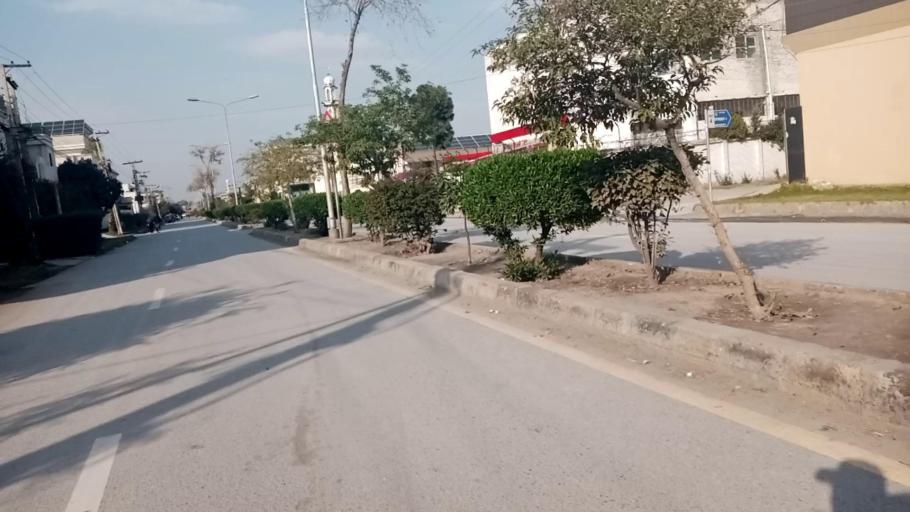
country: PK
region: Khyber Pakhtunkhwa
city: Peshawar
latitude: 33.9864
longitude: 71.4454
